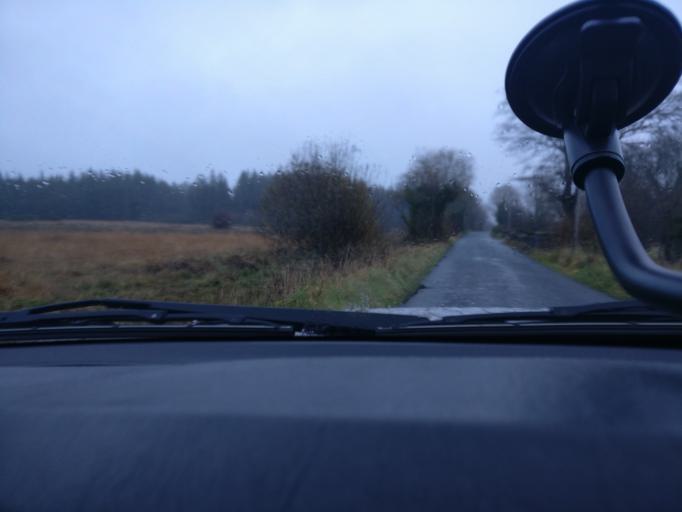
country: IE
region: Connaught
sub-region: County Galway
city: Loughrea
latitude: 53.2311
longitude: -8.5315
